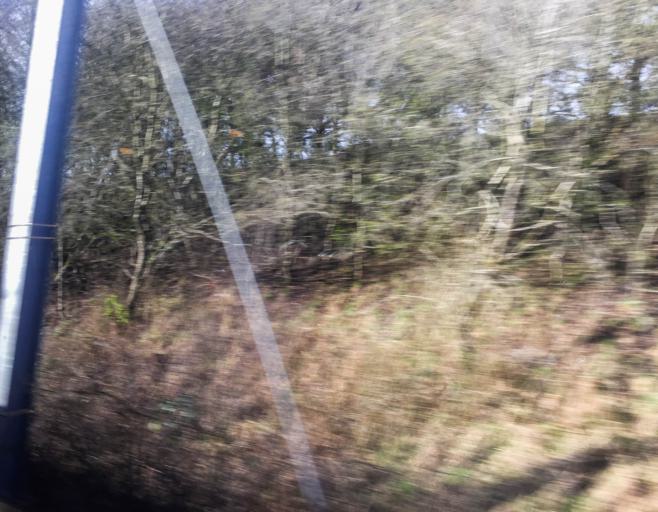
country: GB
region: Scotland
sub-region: North Lanarkshire
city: Stepps
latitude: 55.8905
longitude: -4.1329
